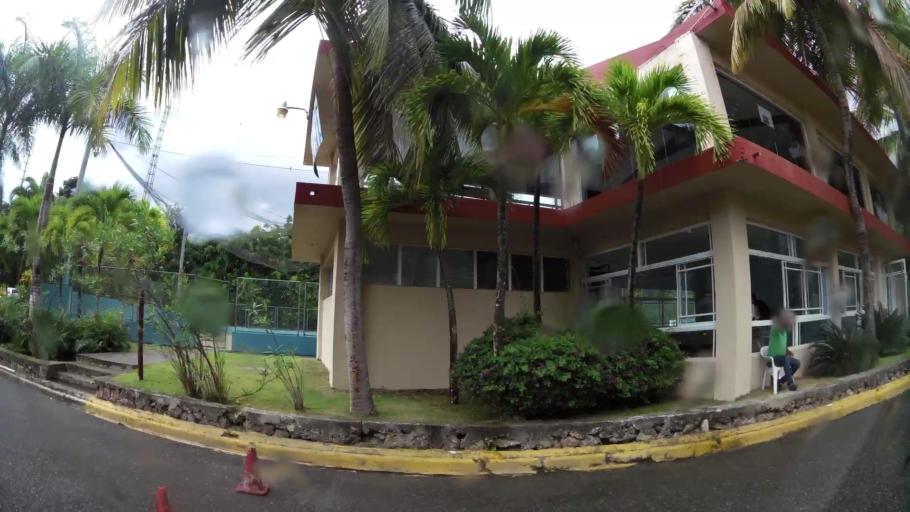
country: DO
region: Nacional
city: La Agustina
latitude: 18.5157
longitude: -69.9336
